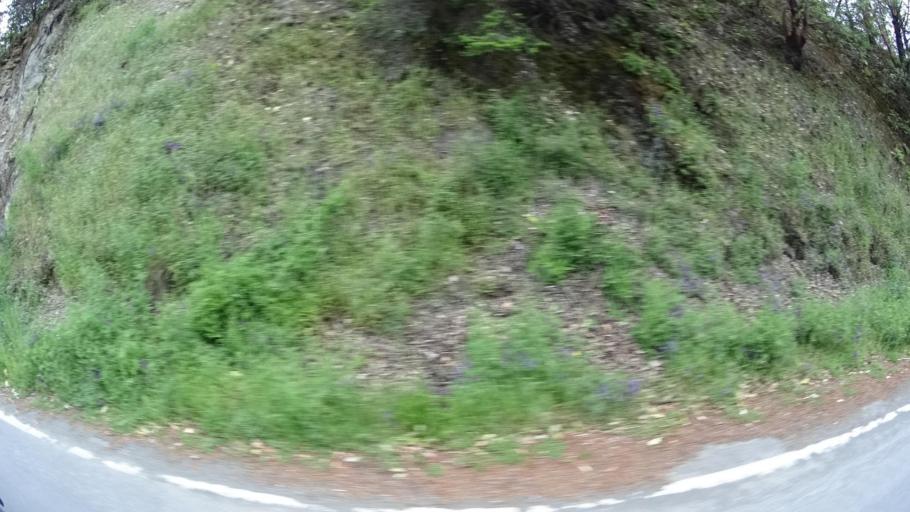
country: US
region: California
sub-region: Humboldt County
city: Willow Creek
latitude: 40.9411
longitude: -123.6267
